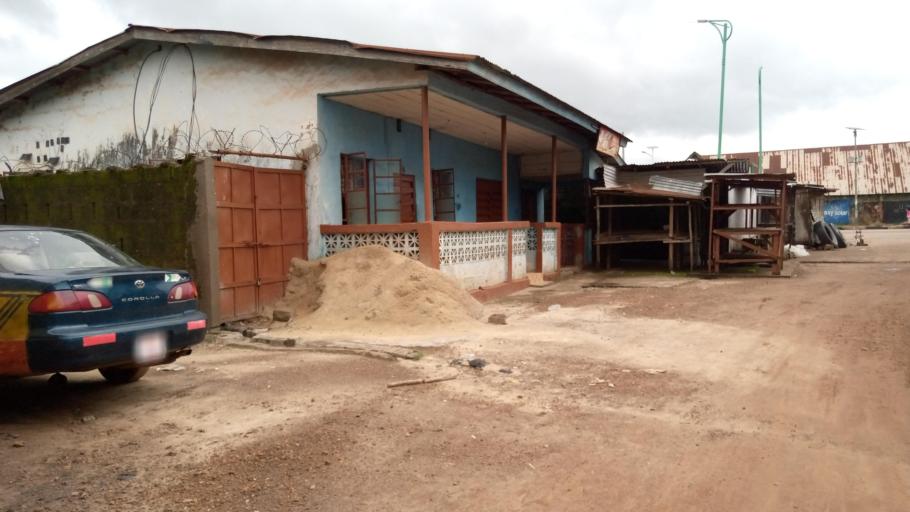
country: SL
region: Southern Province
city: Moyamba
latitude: 8.1595
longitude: -12.4331
